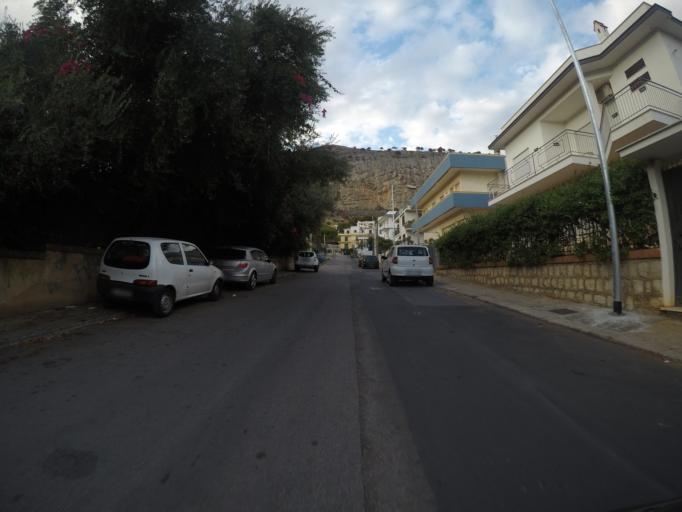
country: IT
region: Sicily
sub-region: Palermo
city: Palermo
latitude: 38.2064
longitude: 13.3237
